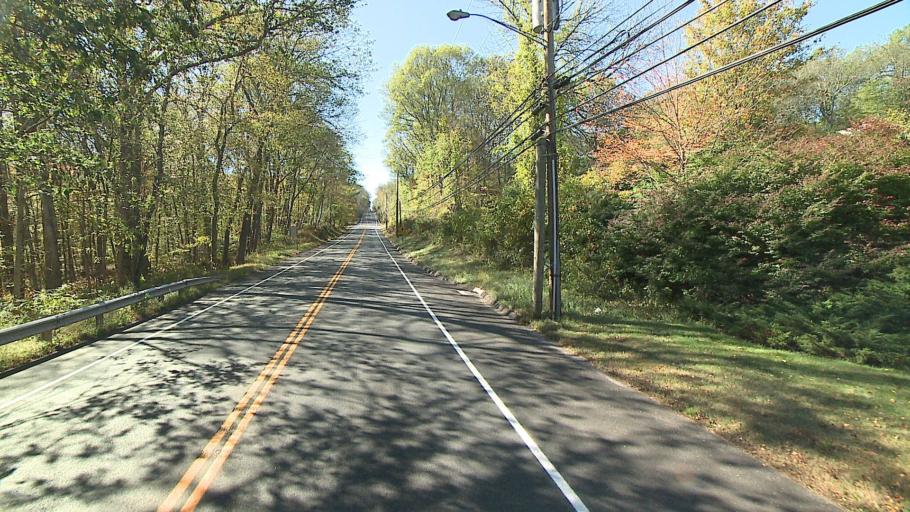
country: US
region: Connecticut
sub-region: Hartford County
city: Terramuggus
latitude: 41.6149
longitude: -72.4736
